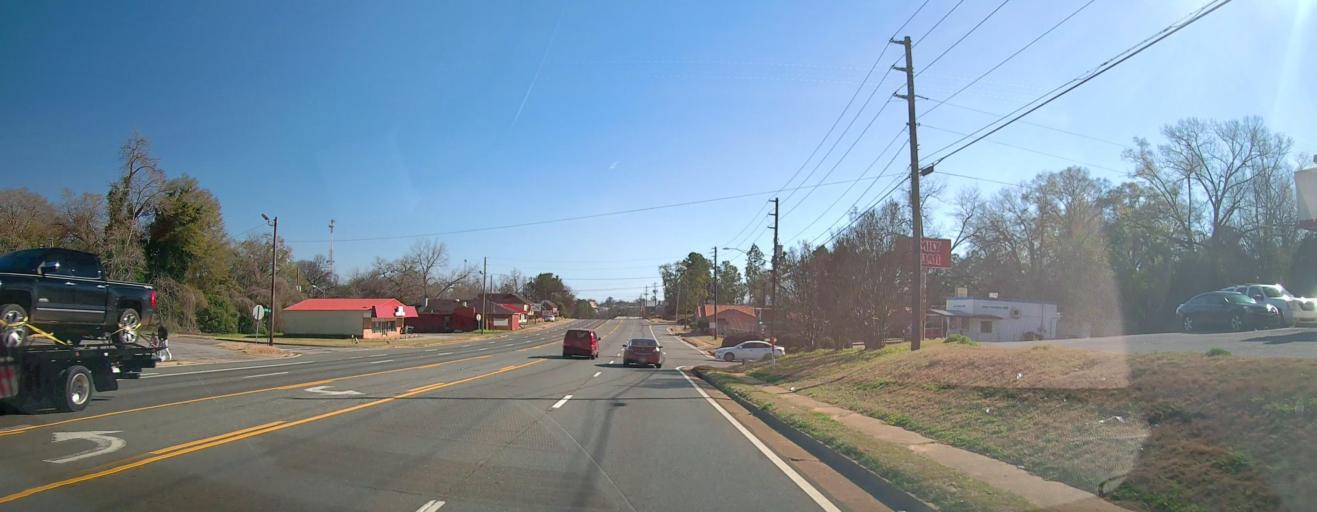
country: US
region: Georgia
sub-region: Sumter County
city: Americus
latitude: 32.0836
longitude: -84.2393
